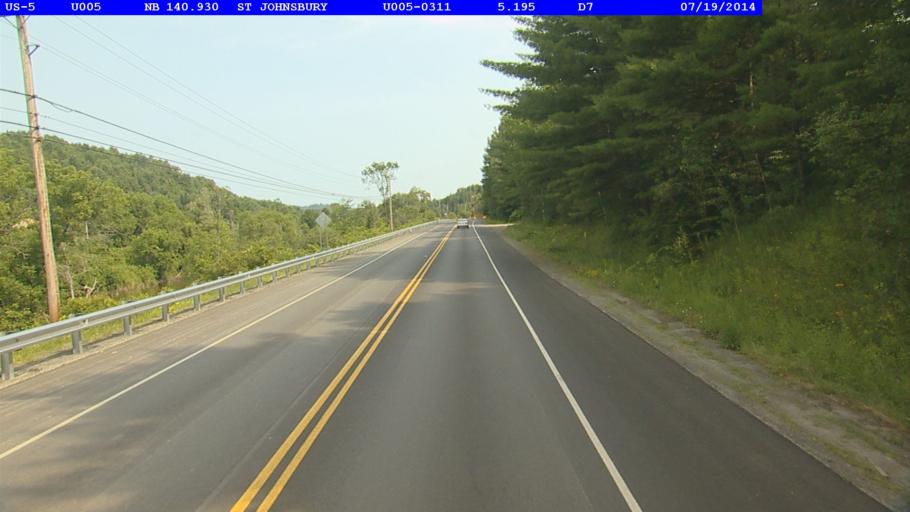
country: US
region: Vermont
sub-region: Caledonia County
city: St Johnsbury
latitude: 44.4658
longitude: -72.0136
